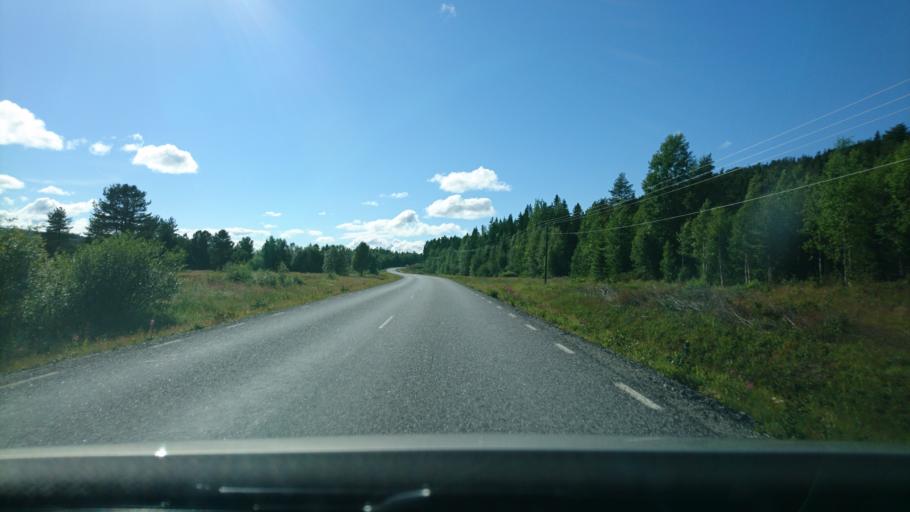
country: SE
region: Vaesterbotten
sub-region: Asele Kommun
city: Asele
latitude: 64.3232
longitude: 17.0900
